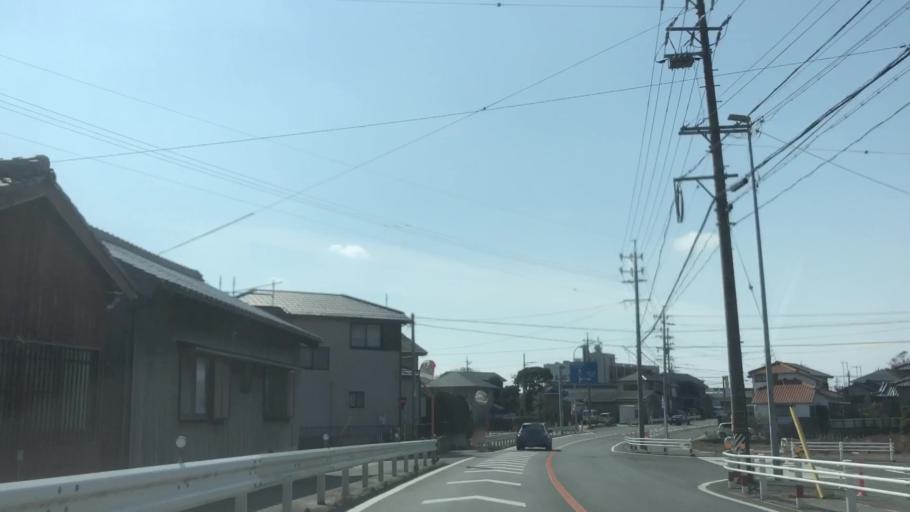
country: JP
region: Aichi
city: Tahara
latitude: 34.6159
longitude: 137.2083
